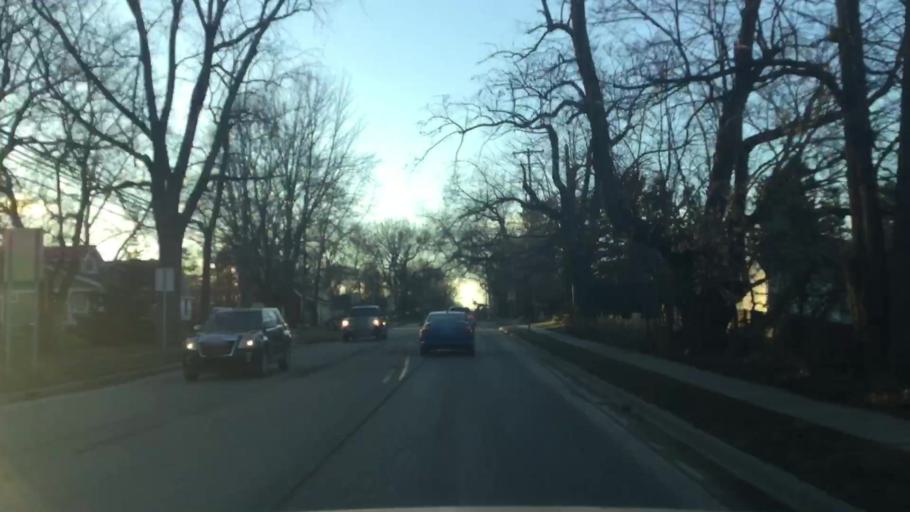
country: US
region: Michigan
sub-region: Genesee County
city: Linden
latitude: 42.8110
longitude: -83.7954
